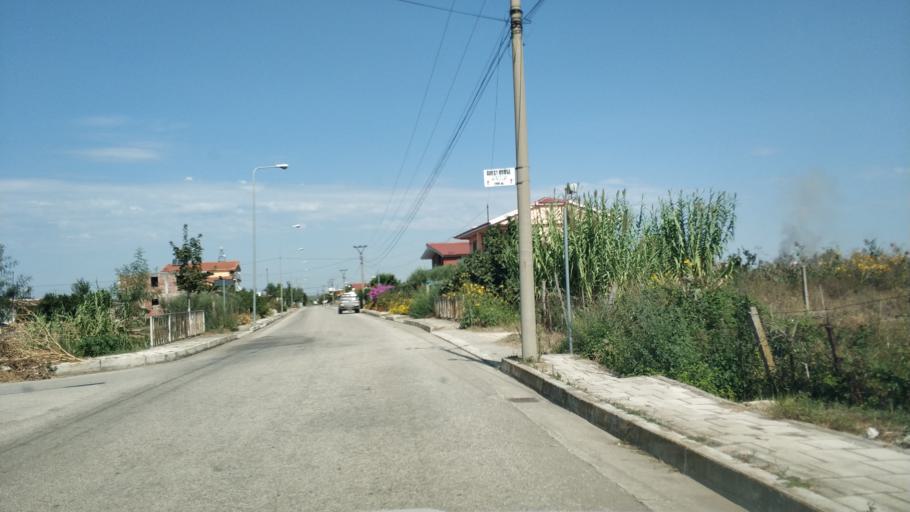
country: AL
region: Fier
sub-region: Rrethi i Lushnjes
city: Divjake
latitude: 40.9994
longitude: 19.5253
